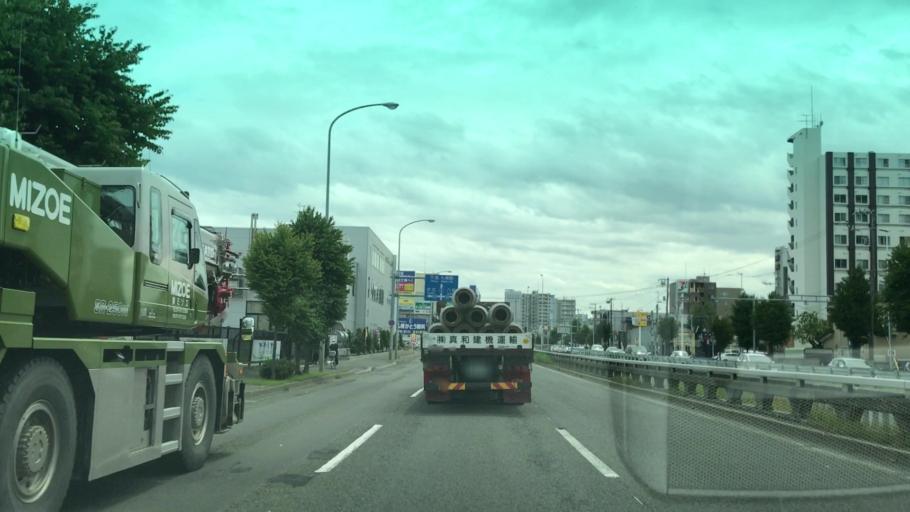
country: JP
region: Hokkaido
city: Sapporo
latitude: 43.0922
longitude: 141.3474
